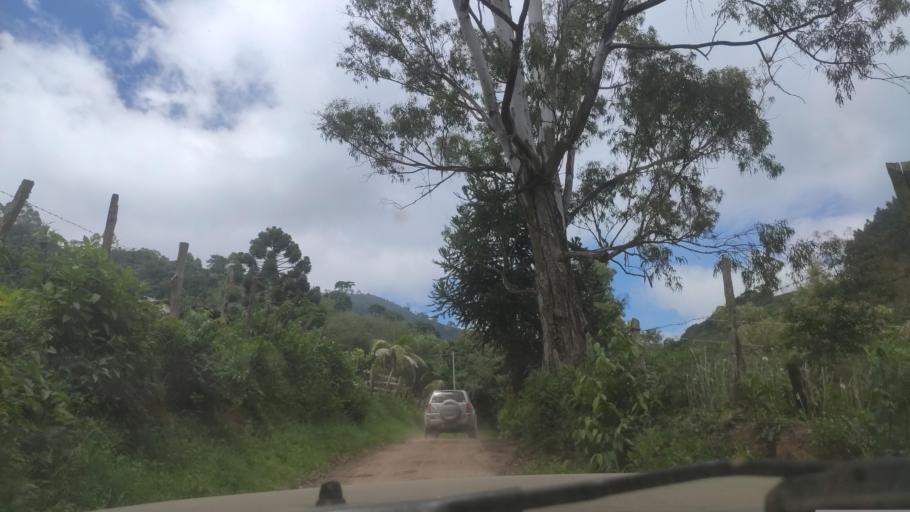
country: BR
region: Minas Gerais
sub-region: Cambui
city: Cambui
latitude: -22.6686
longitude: -45.9319
